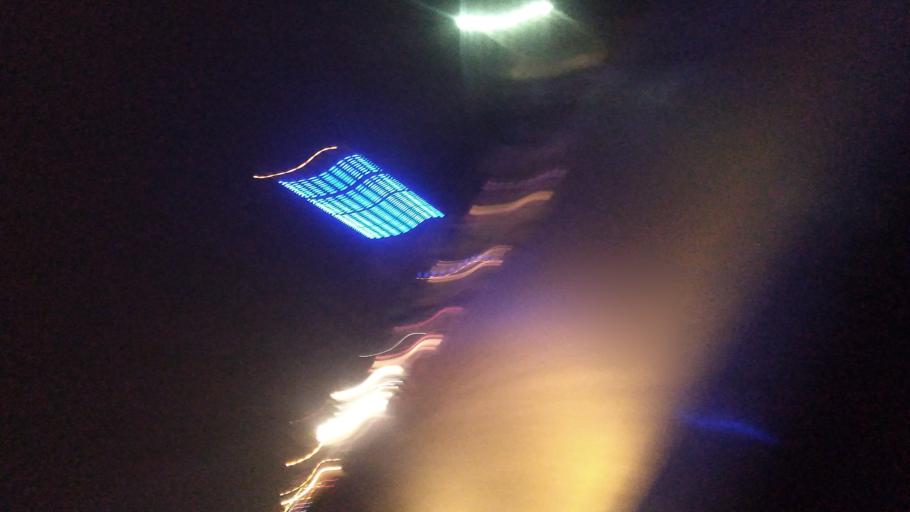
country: IR
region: Khuzestan
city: Ahvaz
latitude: 31.3072
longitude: 48.7538
